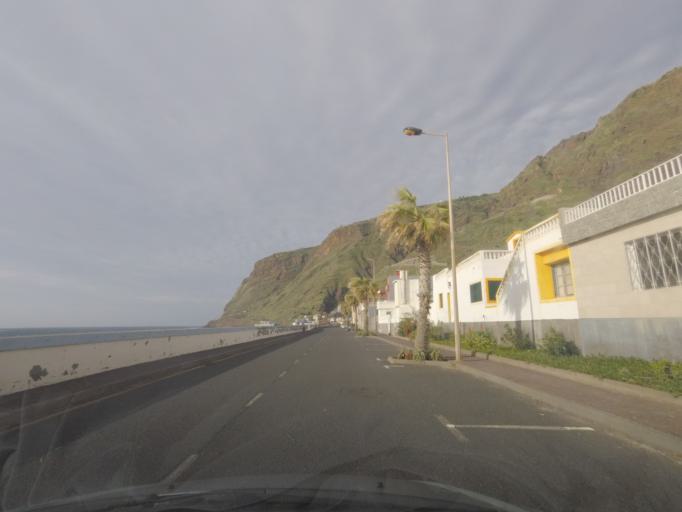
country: PT
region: Madeira
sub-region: Calheta
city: Faja da Ovelha
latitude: 32.7605
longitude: -17.2325
